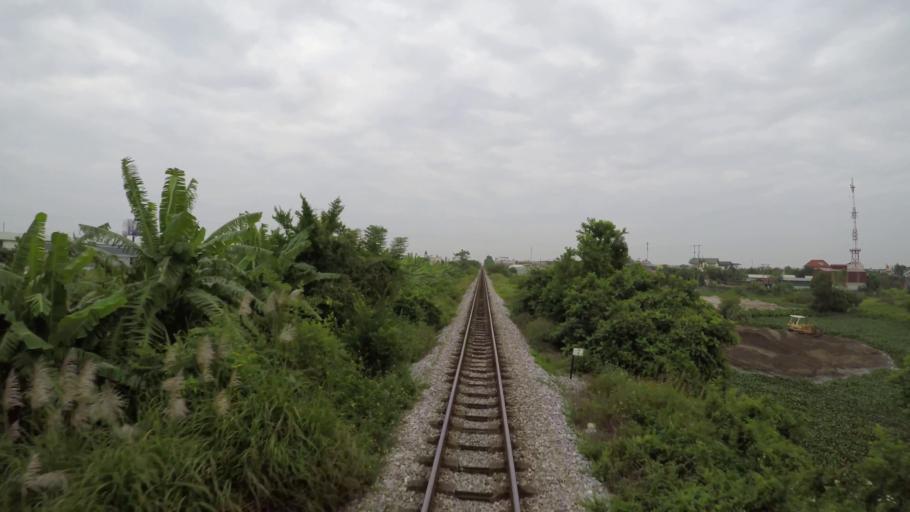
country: VN
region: Hai Duong
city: Thanh Pho Hai Duong
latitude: 20.9471
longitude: 106.3615
